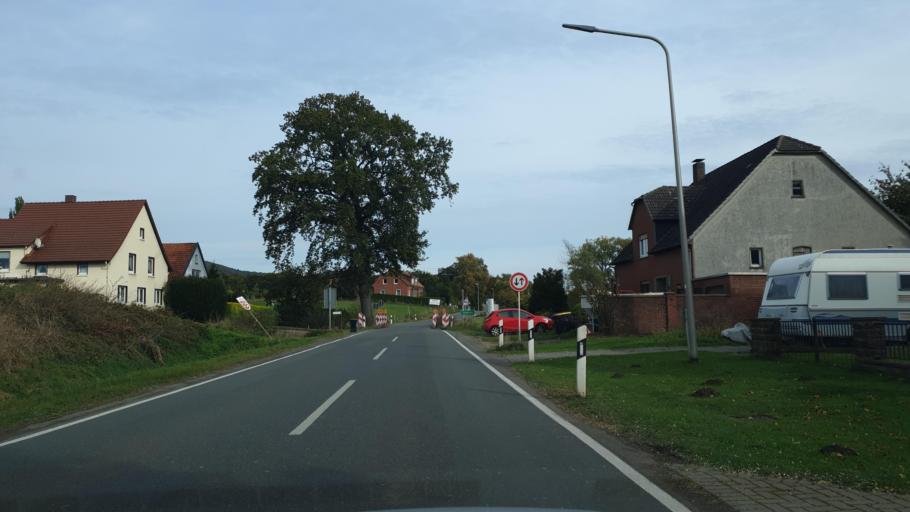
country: DE
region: Lower Saxony
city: Rinteln
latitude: 52.2003
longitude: 9.0438
